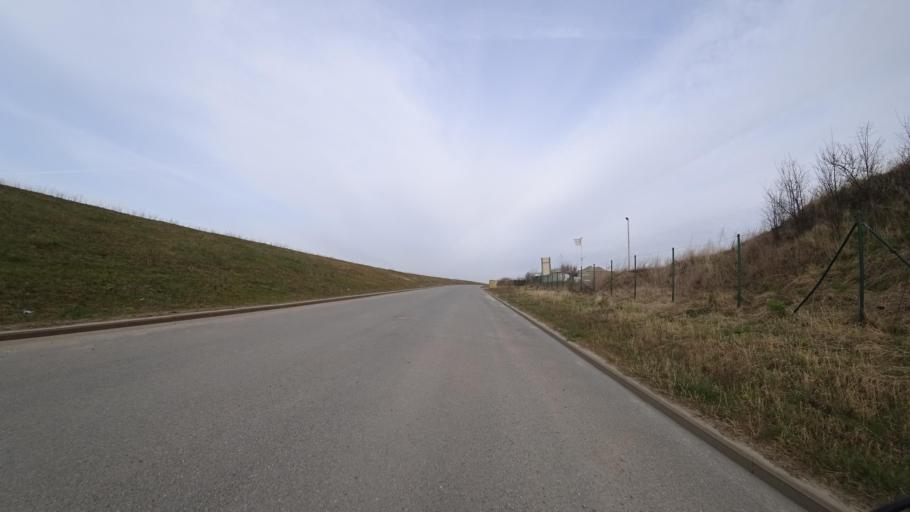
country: BE
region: Wallonia
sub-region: Province du Brabant Wallon
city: Chaumont-Gistoux
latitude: 50.6698
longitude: 4.7134
